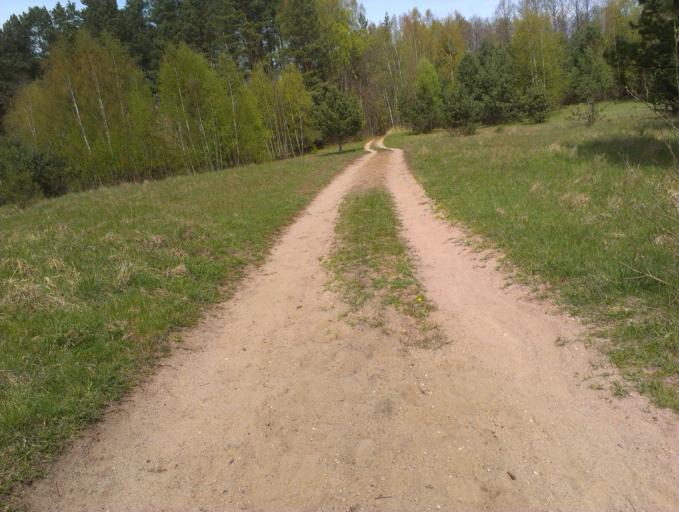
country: PL
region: West Pomeranian Voivodeship
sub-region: Powiat szczecinecki
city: Lubowo
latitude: 53.6245
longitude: 16.3497
